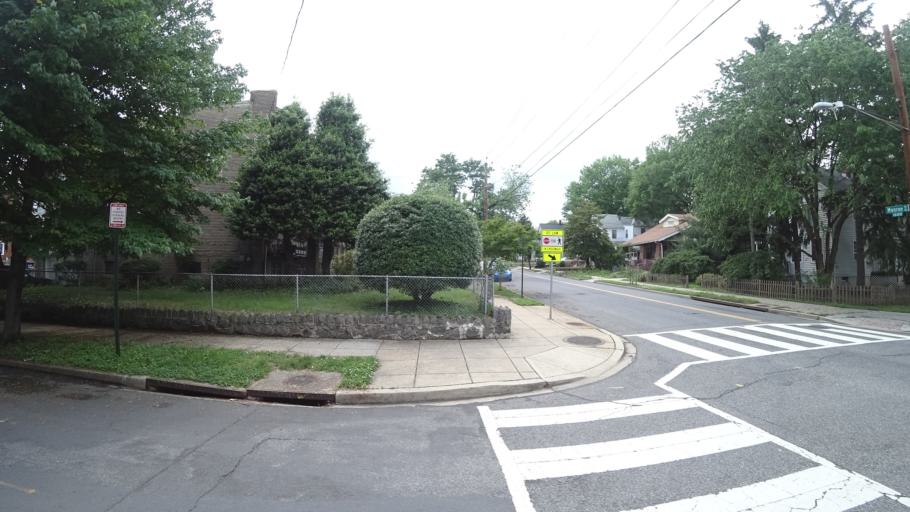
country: US
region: Maryland
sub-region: Prince George's County
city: Mount Rainier
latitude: 38.9329
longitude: -76.9812
